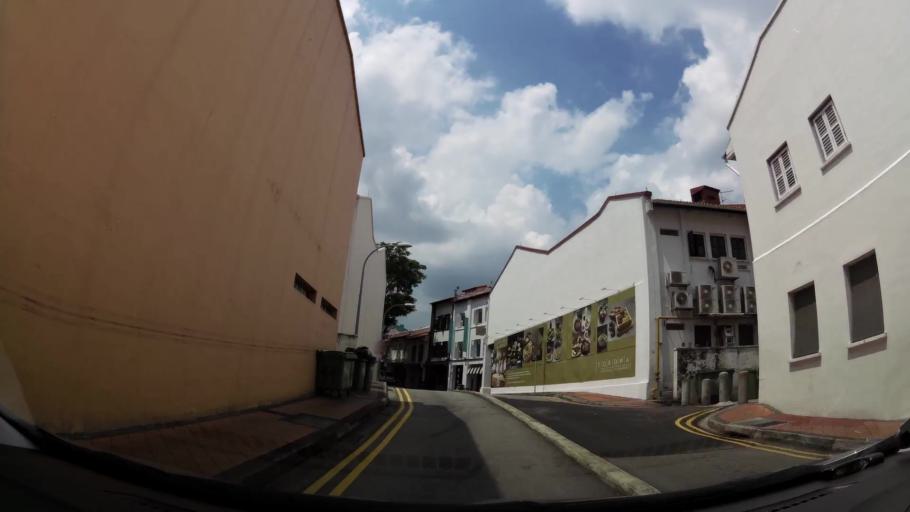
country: SG
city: Singapore
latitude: 1.2794
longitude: 103.8437
